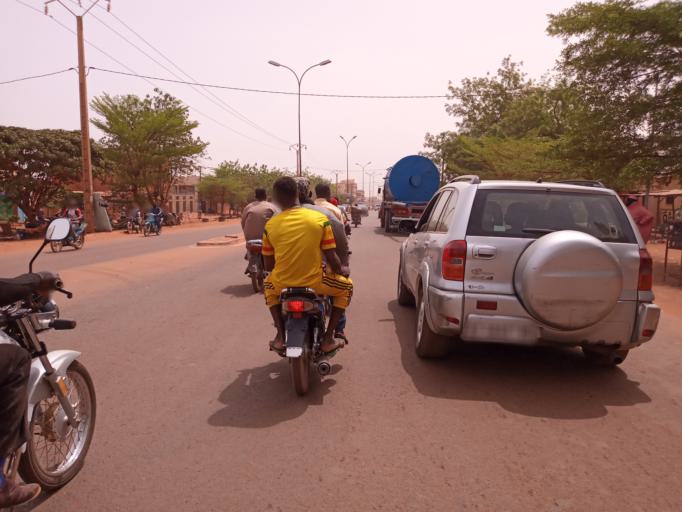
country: ML
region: Bamako
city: Bamako
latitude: 12.6702
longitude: -7.9198
